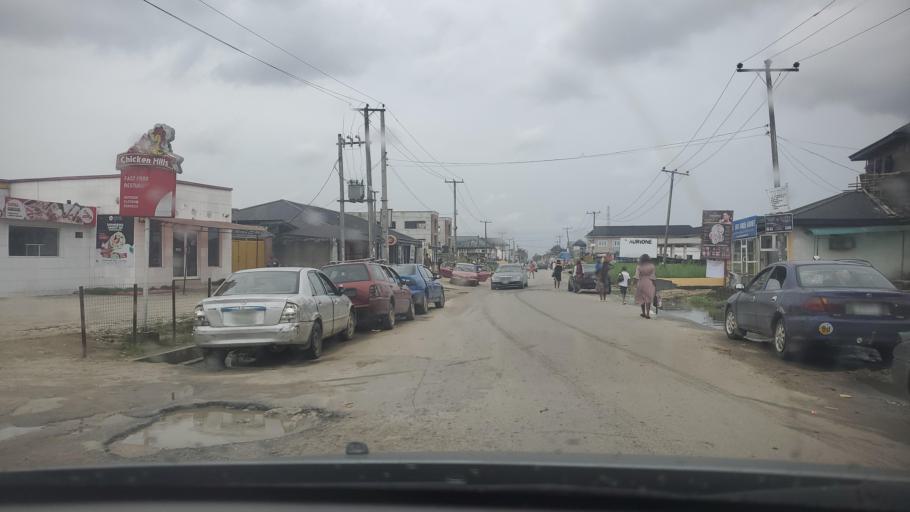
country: NG
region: Rivers
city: Port Harcourt
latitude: 4.8690
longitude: 6.9810
